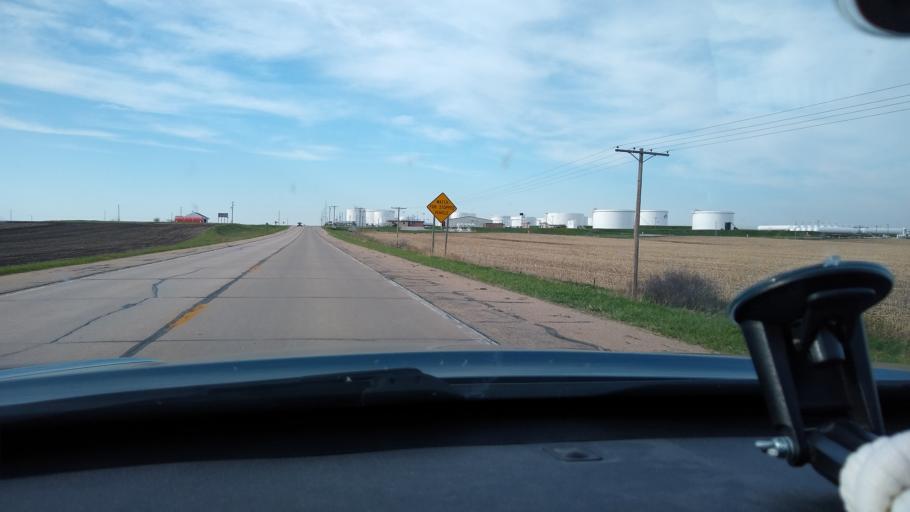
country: US
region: Nebraska
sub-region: Fillmore County
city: Geneva
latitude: 40.5466
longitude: -97.5958
